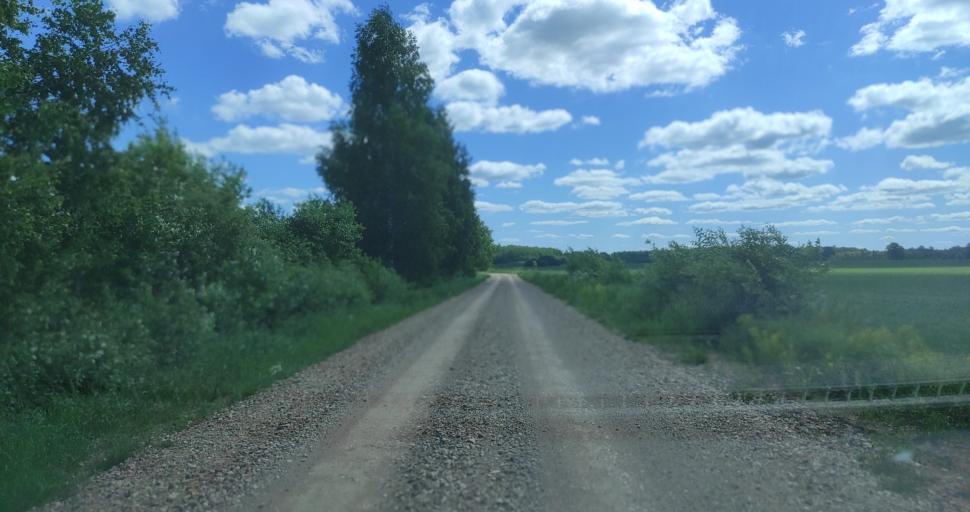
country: LV
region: Aizpute
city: Aizpute
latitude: 56.8469
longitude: 21.6926
